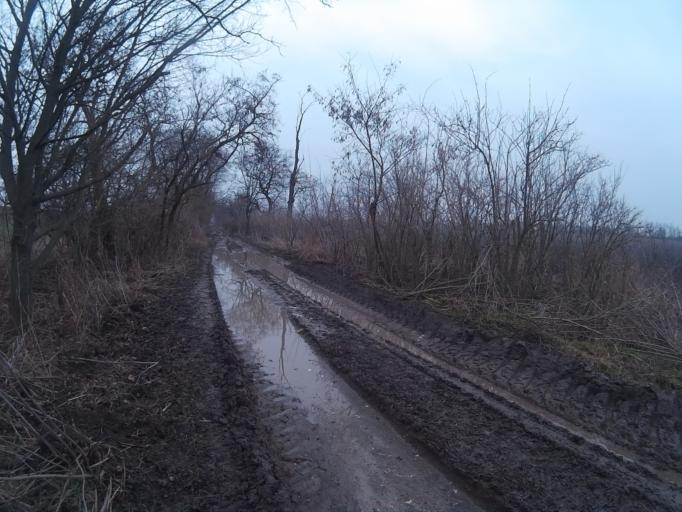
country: HU
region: Fejer
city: Szarliget
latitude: 47.5494
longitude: 18.5642
